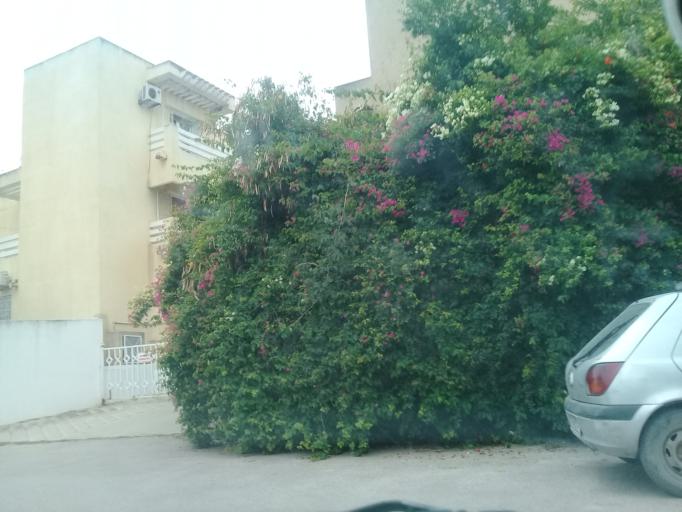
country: TN
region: Tunis
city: Tunis
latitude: 36.8459
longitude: 10.1610
